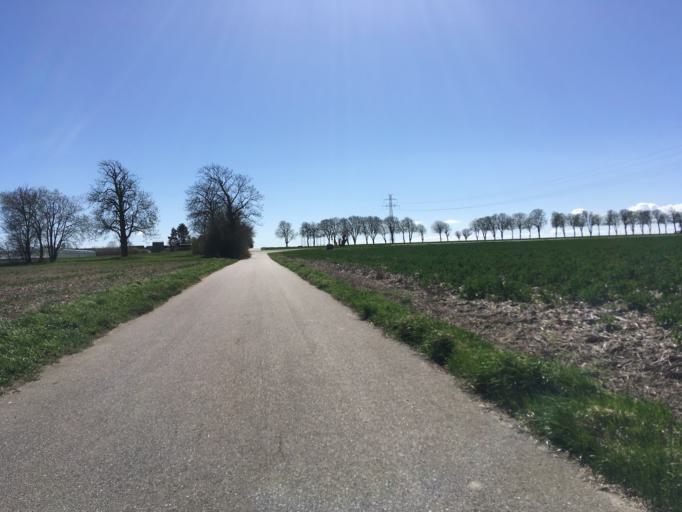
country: SE
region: Skane
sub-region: Lunds Kommun
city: Lund
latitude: 55.6879
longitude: 13.1666
